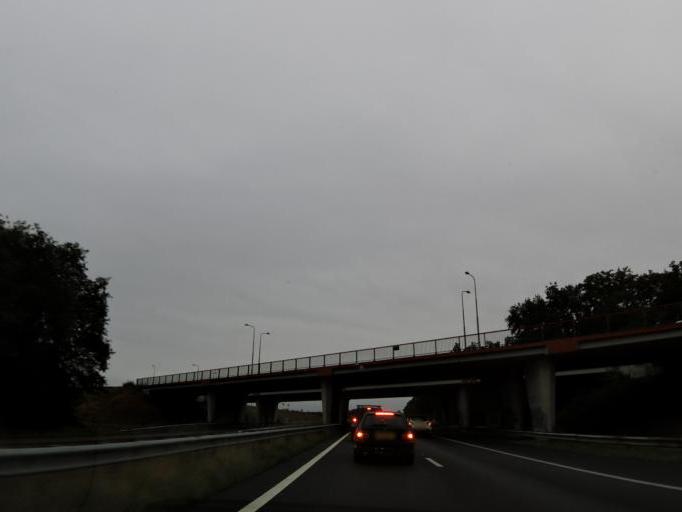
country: NL
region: Limburg
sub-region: Gemeente Leudal
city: Kelpen-Oler
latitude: 51.2348
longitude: 5.7946
